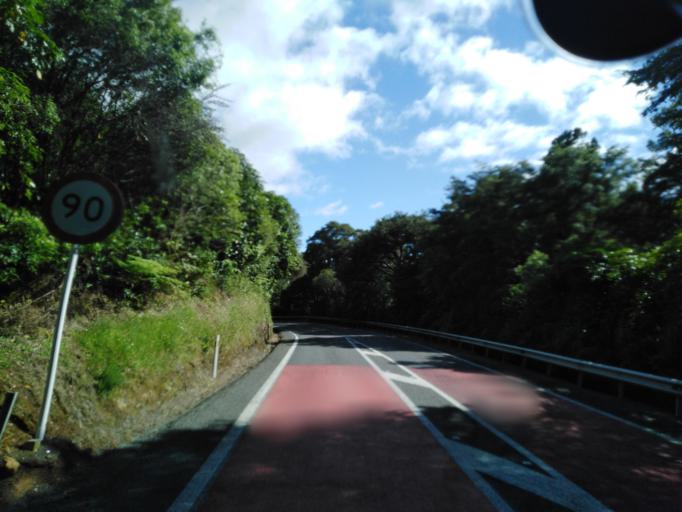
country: NZ
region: Nelson
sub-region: Nelson City
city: Nelson
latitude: -41.2959
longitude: 173.5735
